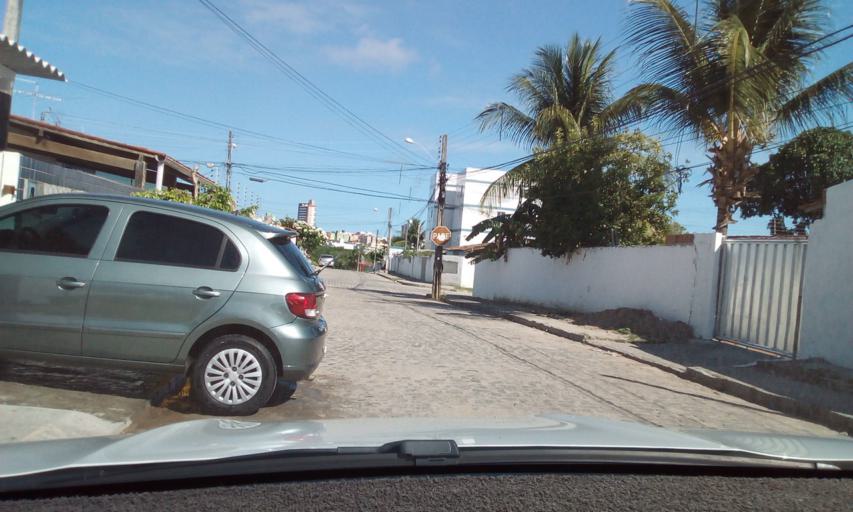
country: BR
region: Paraiba
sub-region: Joao Pessoa
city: Joao Pessoa
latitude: -7.1534
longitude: -34.8478
